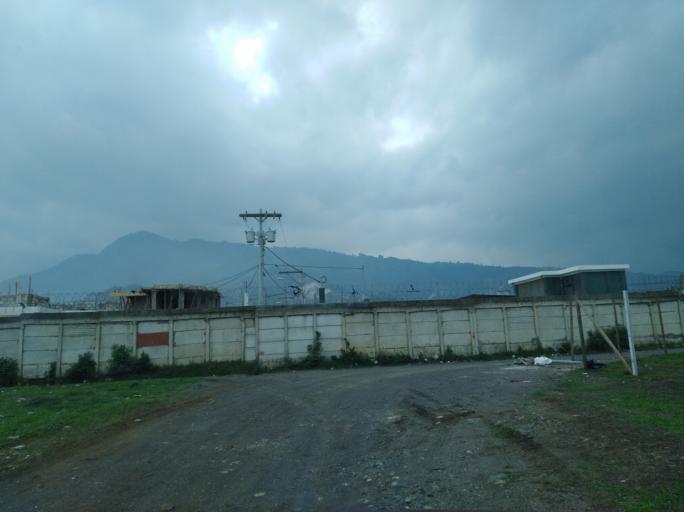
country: GT
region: Guatemala
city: Villa Nueva
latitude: 14.5261
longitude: -90.6246
